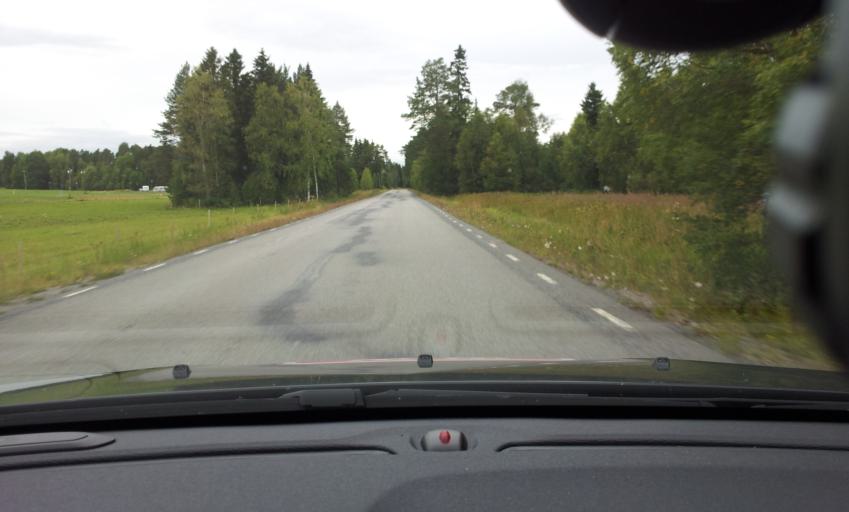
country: SE
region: Jaemtland
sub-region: OEstersunds Kommun
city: Brunflo
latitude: 63.0499
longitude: 14.8583
